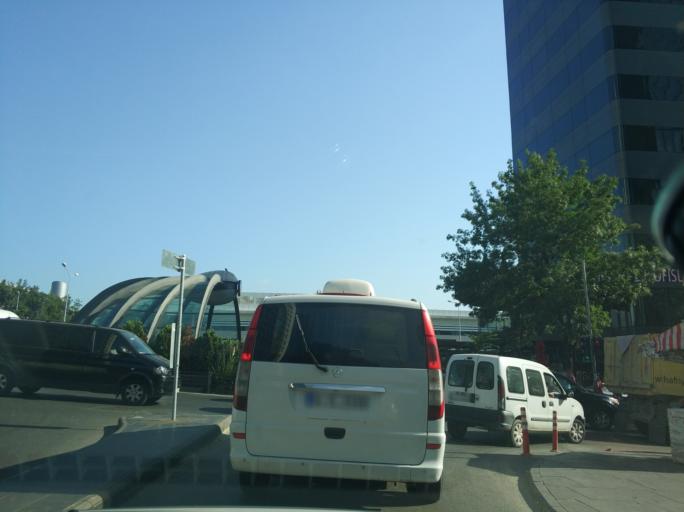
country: TR
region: Istanbul
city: Sisli
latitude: 41.1088
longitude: 29.0199
